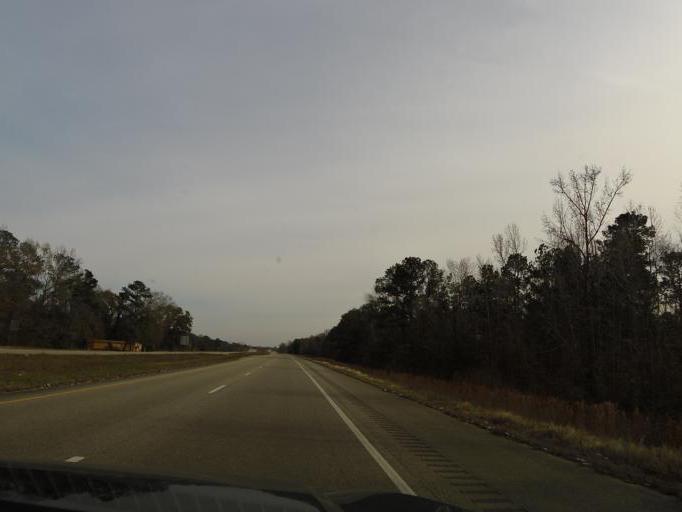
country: US
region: Alabama
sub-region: Houston County
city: Ashford
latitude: 31.1255
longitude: -85.0653
